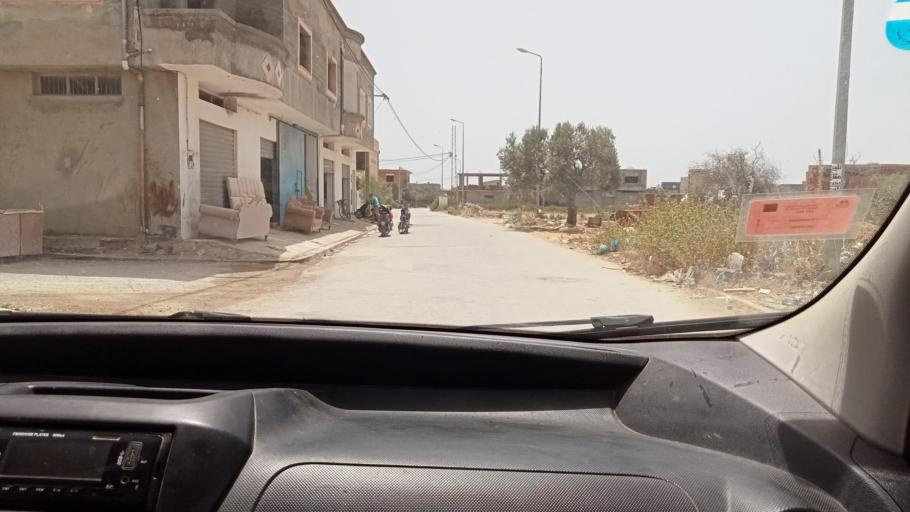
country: TN
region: Nabul
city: Qulaybiyah
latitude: 36.8588
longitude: 11.0855
